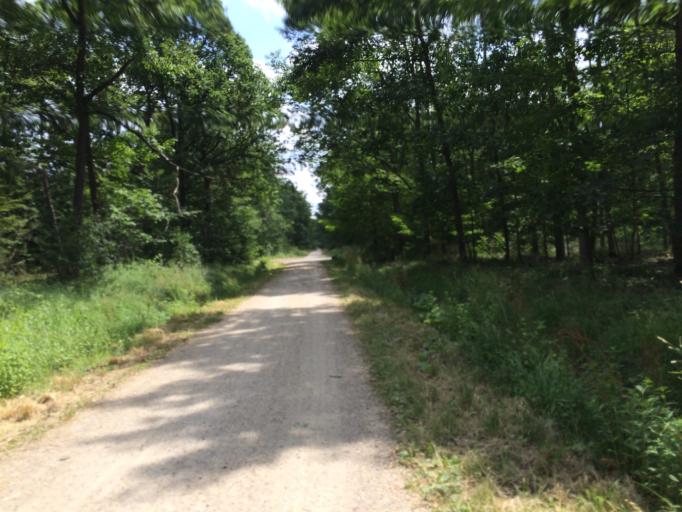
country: FR
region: Ile-de-France
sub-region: Departement de l'Essonne
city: Tigery
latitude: 48.6632
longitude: 2.5061
